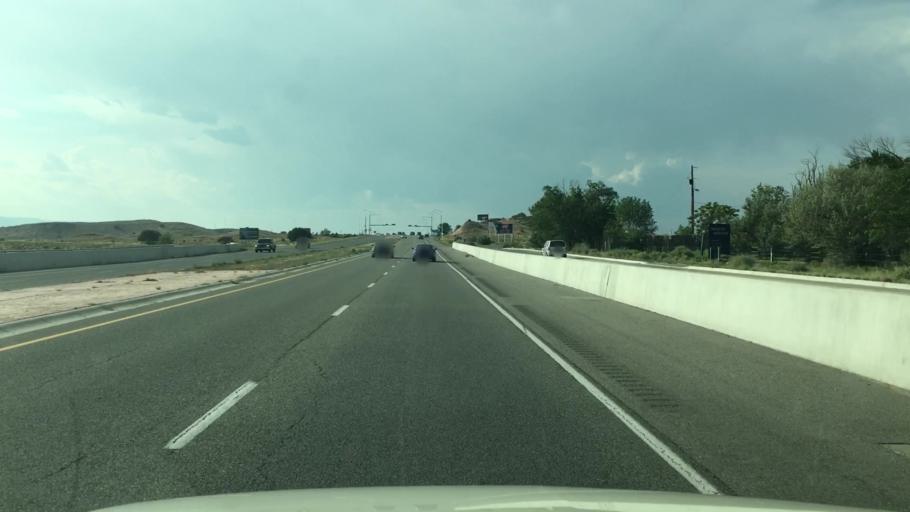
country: US
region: New Mexico
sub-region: Santa Fe County
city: El Valle de Arroyo Seco
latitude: 35.9722
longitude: -106.0407
